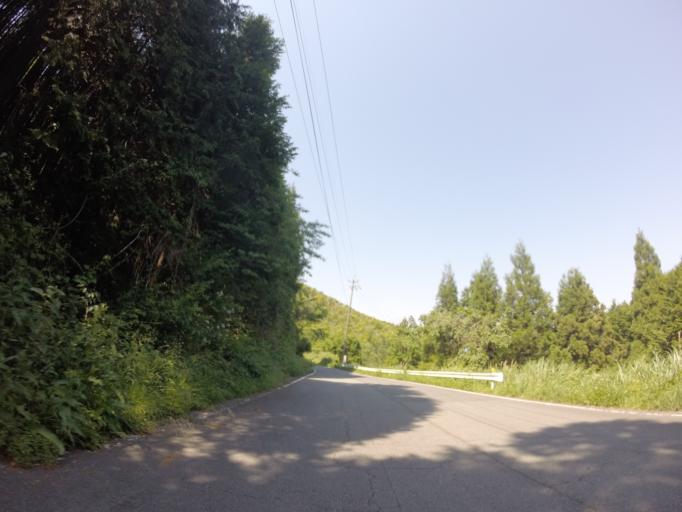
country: JP
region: Shizuoka
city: Fujinomiya
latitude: 35.1571
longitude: 138.5684
